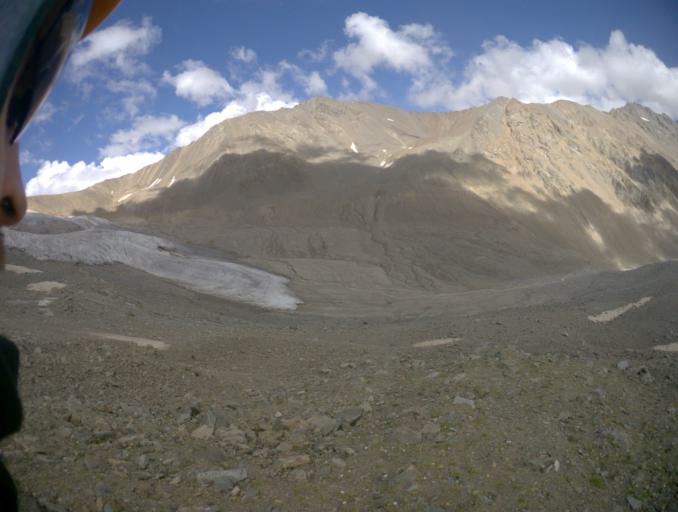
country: RU
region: Kabardino-Balkariya
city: Terskol
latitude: 43.3325
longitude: 42.5450
